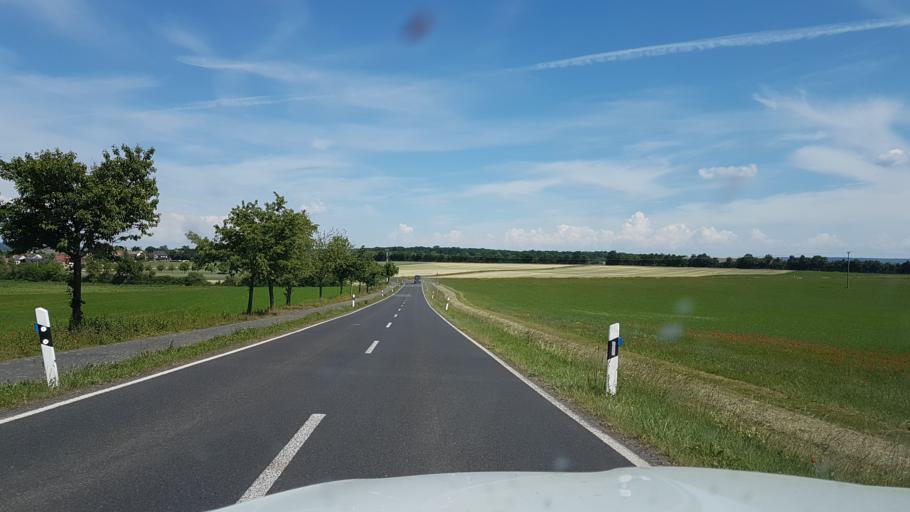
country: DE
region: Bavaria
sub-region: Regierungsbezirk Unterfranken
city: Knetzgau
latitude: 49.9912
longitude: 10.5078
